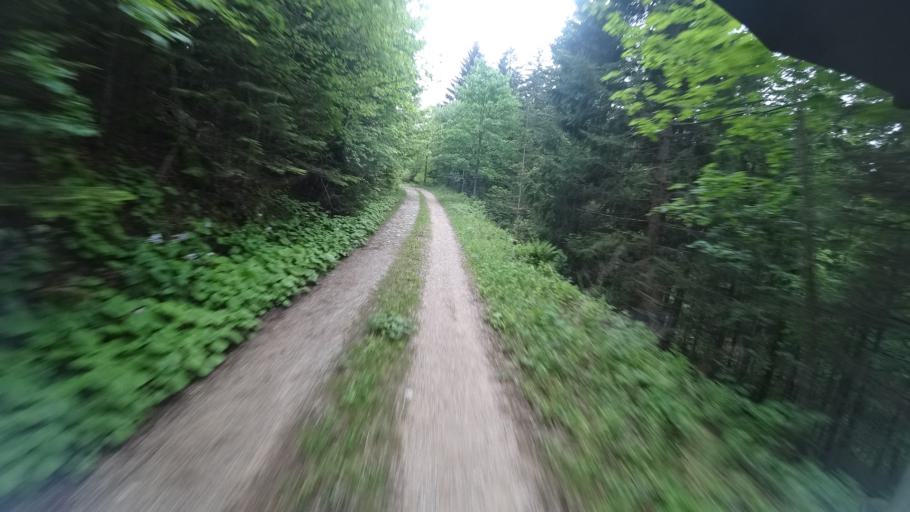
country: BA
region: Federation of Bosnia and Herzegovina
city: Bihac
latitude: 44.6356
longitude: 15.8197
